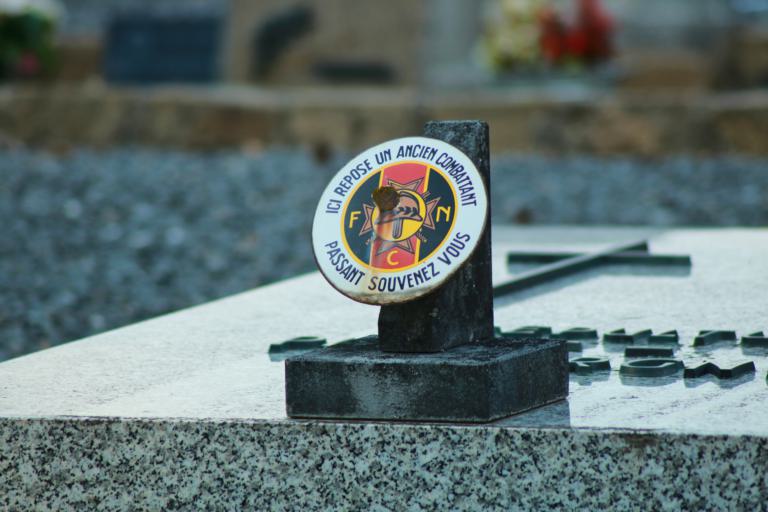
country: BE
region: Wallonia
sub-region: Province du Luxembourg
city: Daverdisse
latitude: 49.9785
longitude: 5.0869
